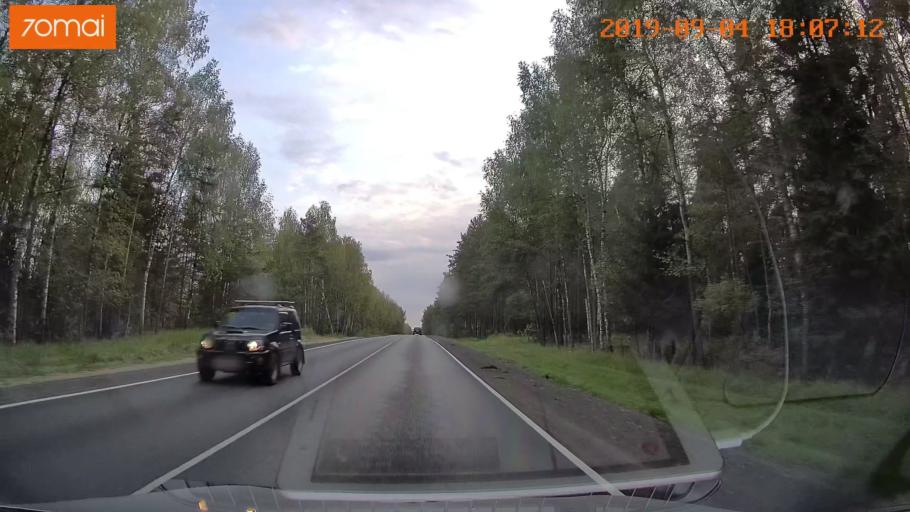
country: RU
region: Moskovskaya
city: Khorlovo
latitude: 55.4221
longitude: 38.8044
